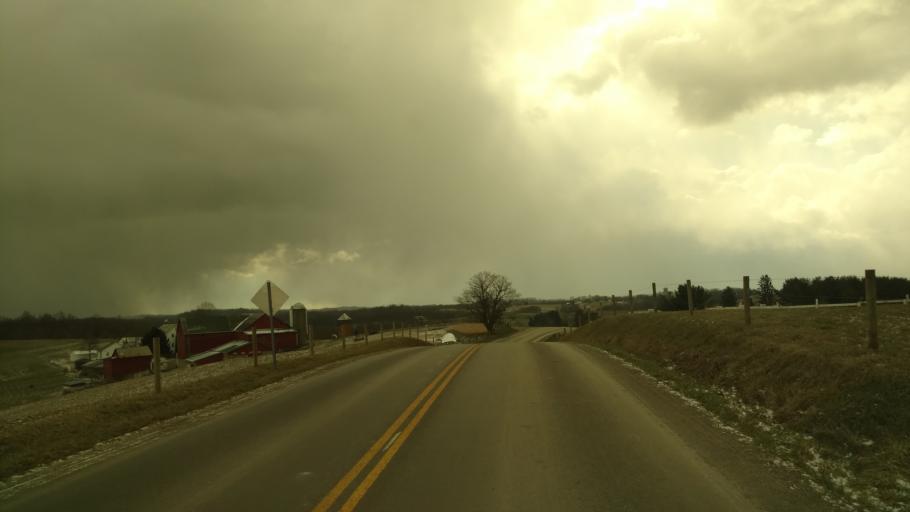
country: US
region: Ohio
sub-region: Tuscarawas County
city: Sugarcreek
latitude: 40.4711
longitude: -81.7799
